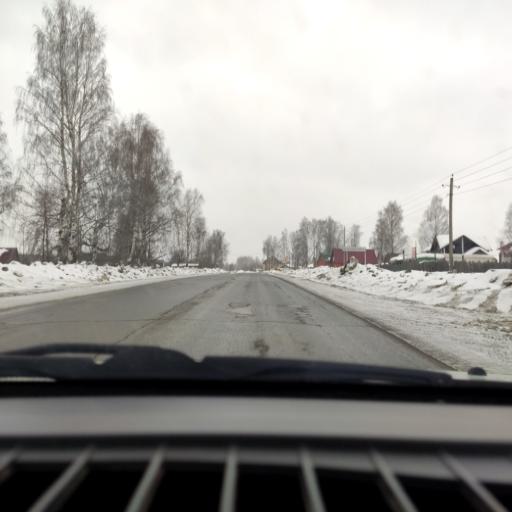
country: RU
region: Perm
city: Krasnokamsk
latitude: 58.0985
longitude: 55.8097
